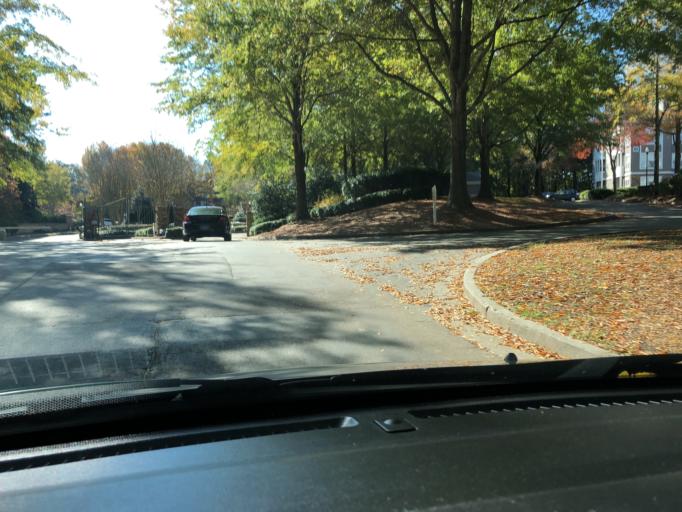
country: US
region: Georgia
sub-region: Fulton County
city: Johns Creek
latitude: 34.0163
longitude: -84.1833
